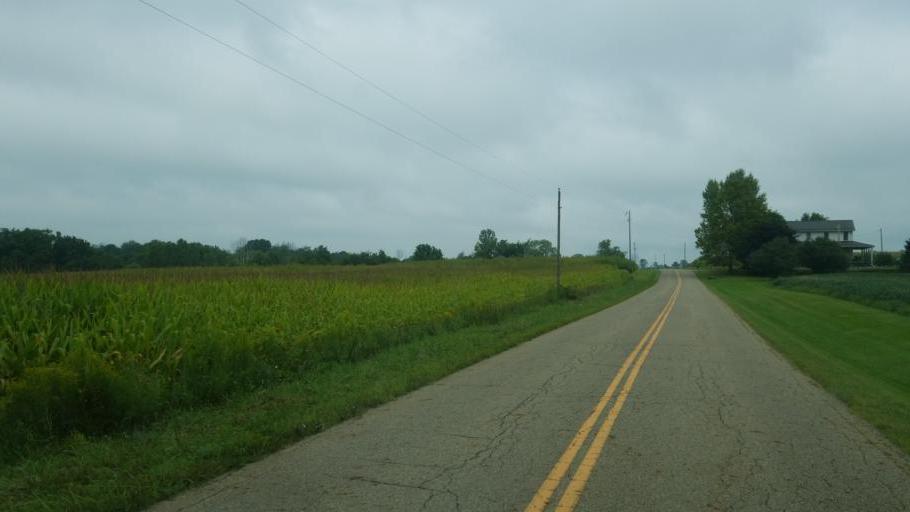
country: US
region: Ohio
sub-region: Licking County
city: Utica
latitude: 40.2745
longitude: -82.4159
